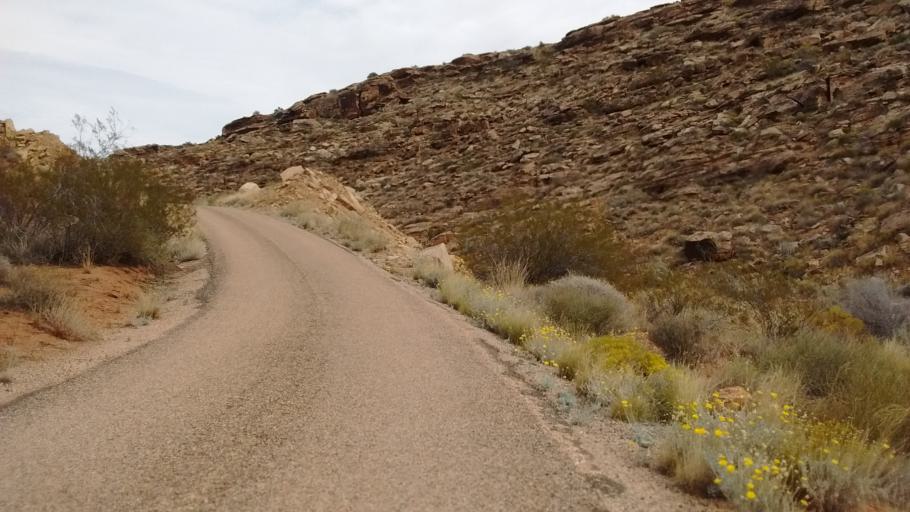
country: US
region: Utah
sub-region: Washington County
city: Washington
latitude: 37.1286
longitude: -113.4732
